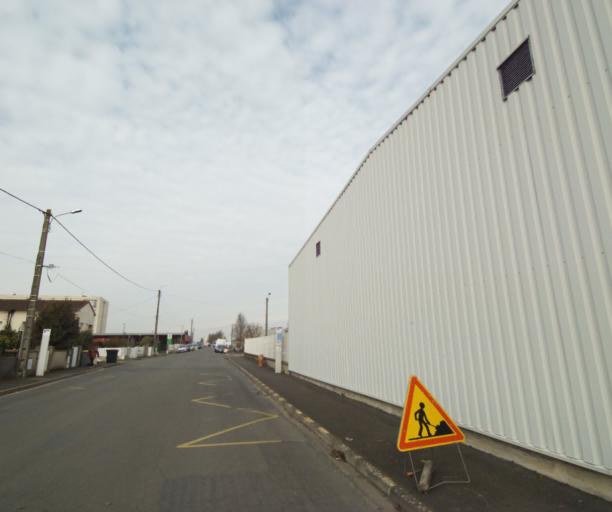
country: FR
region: Poitou-Charentes
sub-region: Departement des Deux-Sevres
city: Niort
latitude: 46.3118
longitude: -0.4394
